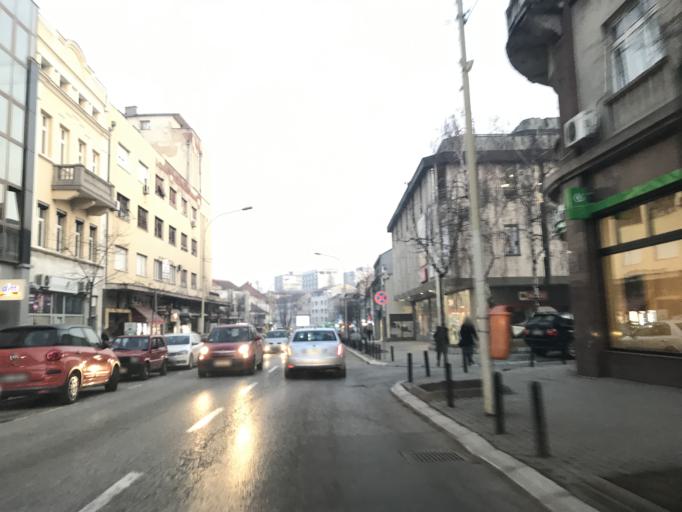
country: RS
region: Central Serbia
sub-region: Sumadijski Okrug
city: Kragujevac
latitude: 44.0117
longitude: 20.9133
